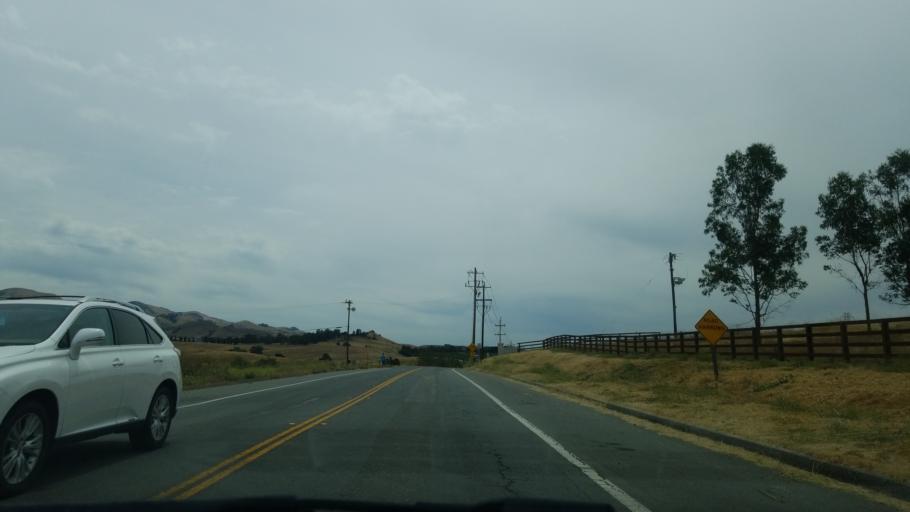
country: US
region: California
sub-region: San Luis Obispo County
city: San Luis Obispo
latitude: 35.2484
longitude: -120.6187
